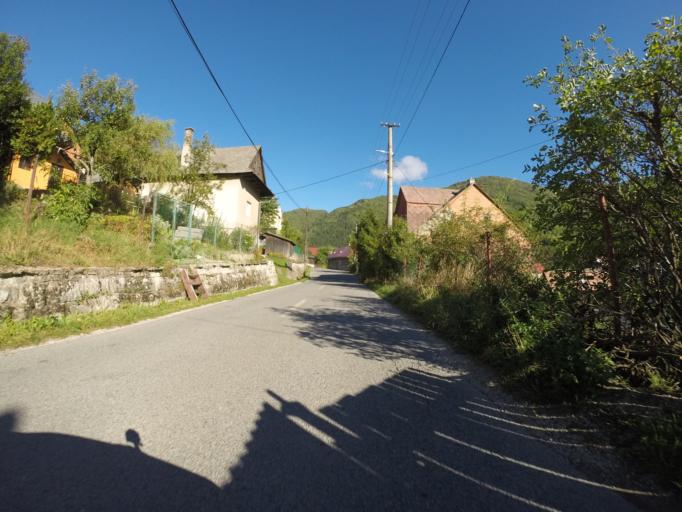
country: SK
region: Trenciansky
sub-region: Okres Povazska Bystrica
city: Povazska Bystrica
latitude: 48.9593
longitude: 18.4106
